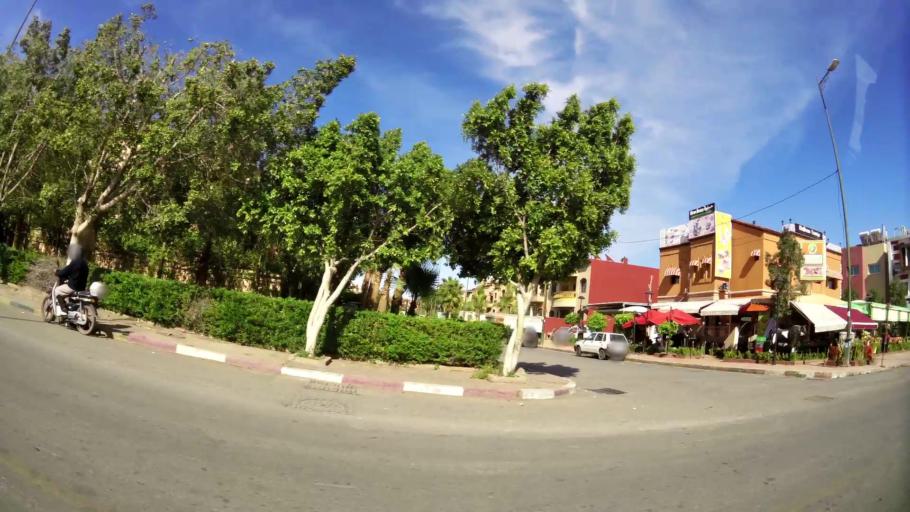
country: MA
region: Marrakech-Tensift-Al Haouz
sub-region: Marrakech
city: Marrakesh
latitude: 31.6501
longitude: -8.0489
